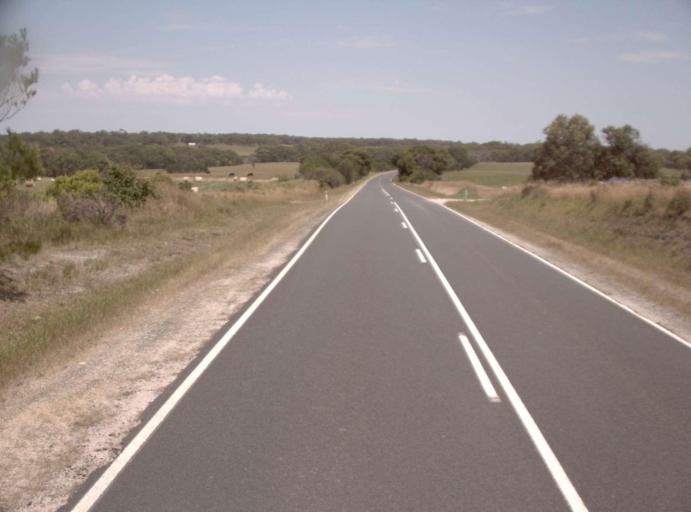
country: AU
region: Victoria
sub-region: Bass Coast
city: North Wonthaggi
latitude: -38.6687
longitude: 145.9217
